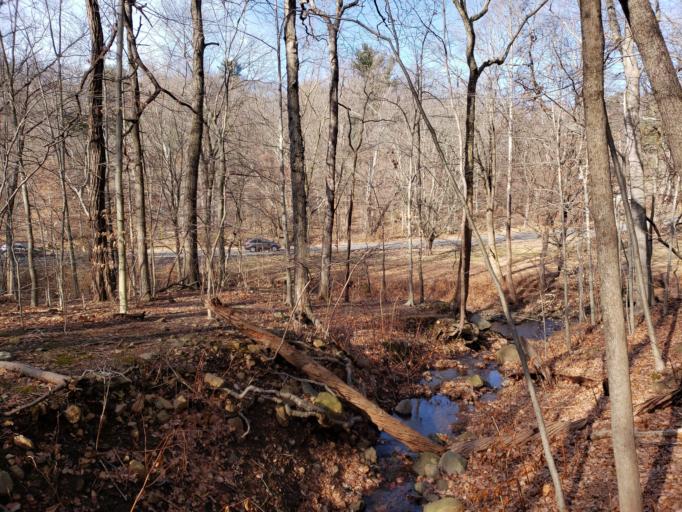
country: US
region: New Jersey
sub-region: Essex County
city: Short Hills
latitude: 40.7351
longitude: -74.3056
